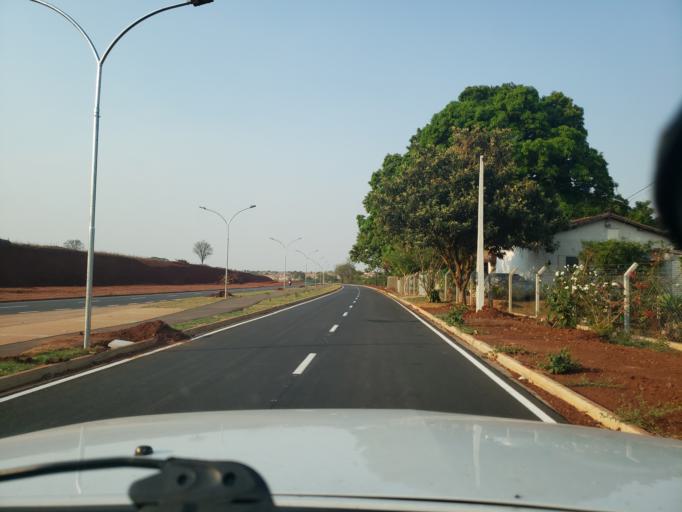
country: BR
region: Sao Paulo
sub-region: Moji-Guacu
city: Mogi-Gaucu
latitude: -22.3233
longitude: -46.9483
